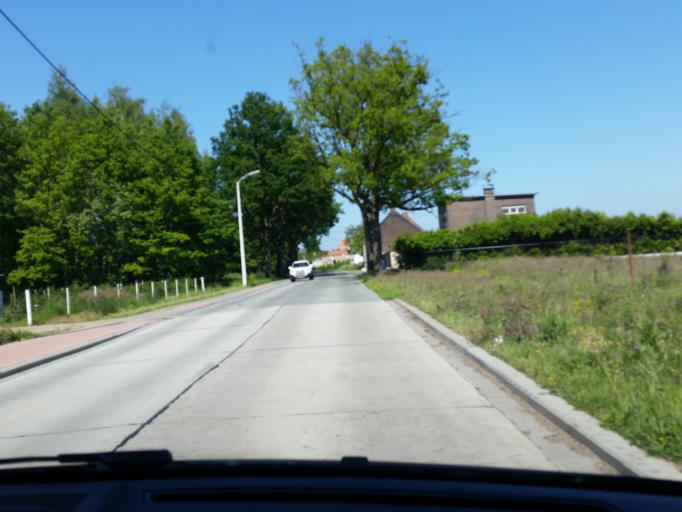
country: BE
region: Flanders
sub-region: Provincie Antwerpen
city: Bonheiden
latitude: 51.0426
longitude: 4.5543
